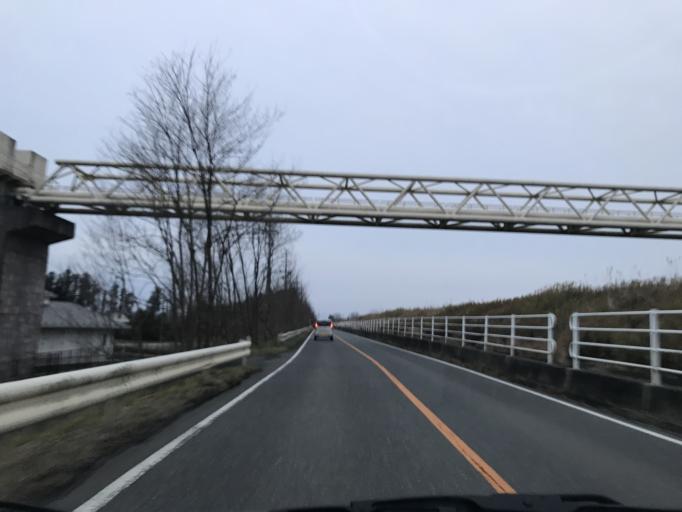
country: JP
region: Iwate
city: Ichinoseki
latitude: 38.7548
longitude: 141.1396
